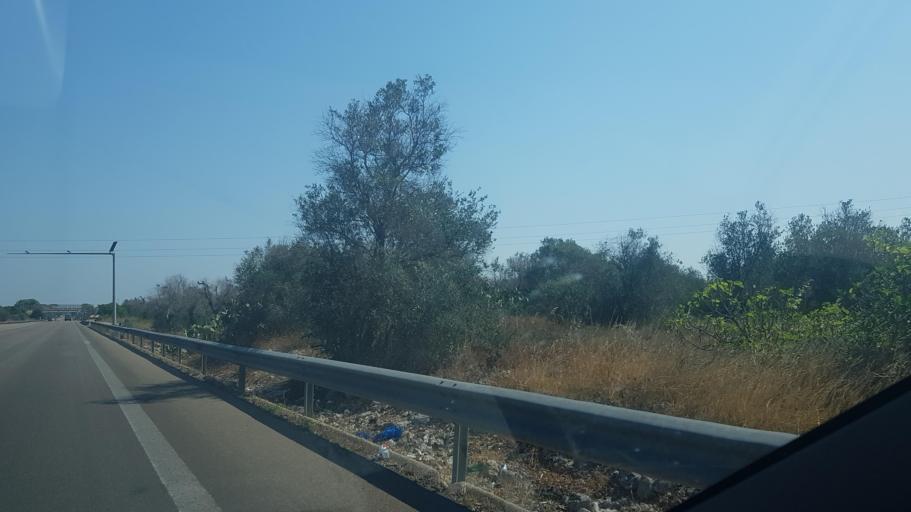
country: IT
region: Apulia
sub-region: Provincia di Lecce
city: Scorrano
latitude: 40.0915
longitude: 18.3110
